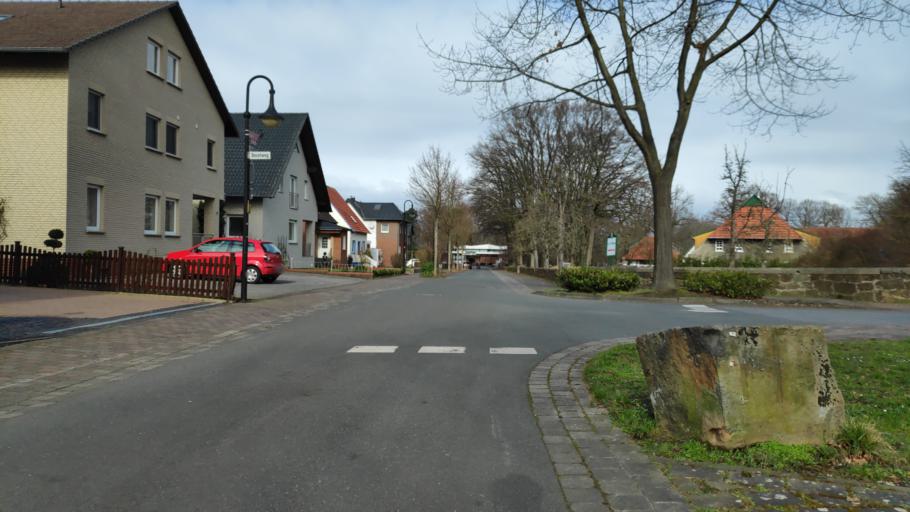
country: DE
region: North Rhine-Westphalia
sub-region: Regierungsbezirk Detmold
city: Hille
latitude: 52.2764
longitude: 8.7875
